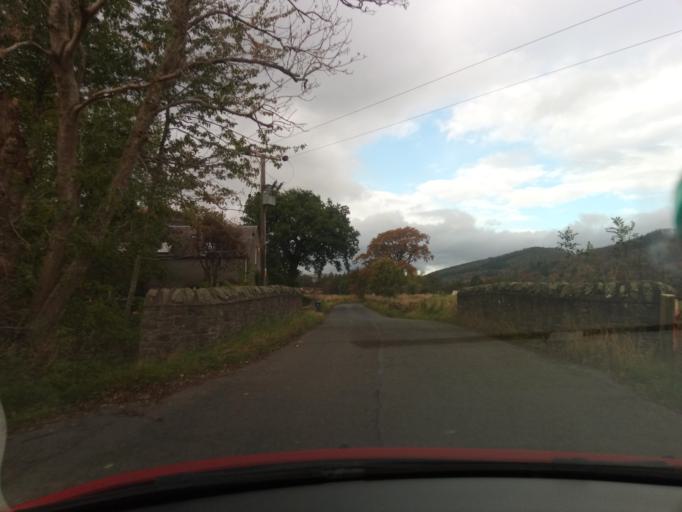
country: GB
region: Scotland
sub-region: The Scottish Borders
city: Peebles
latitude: 55.6420
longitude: -3.1612
